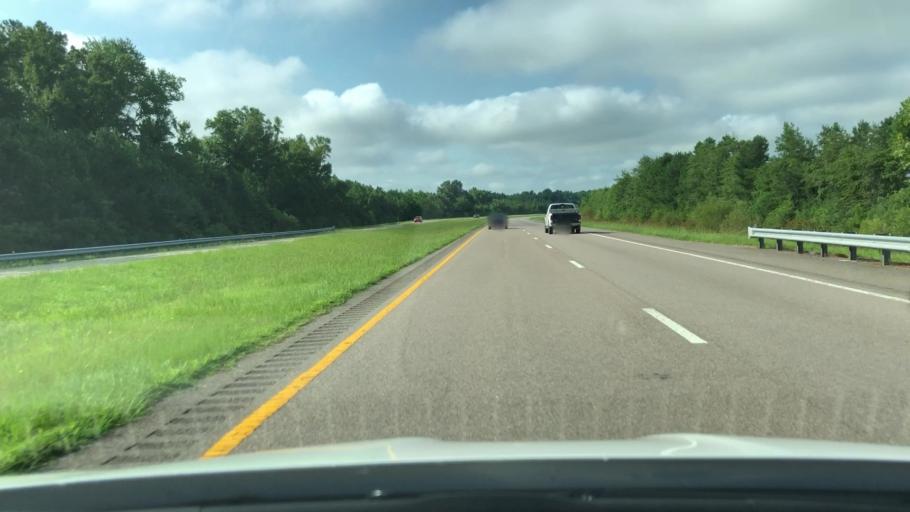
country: US
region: Virginia
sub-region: City of Portsmouth
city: Portsmouth Heights
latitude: 36.6570
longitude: -76.3545
